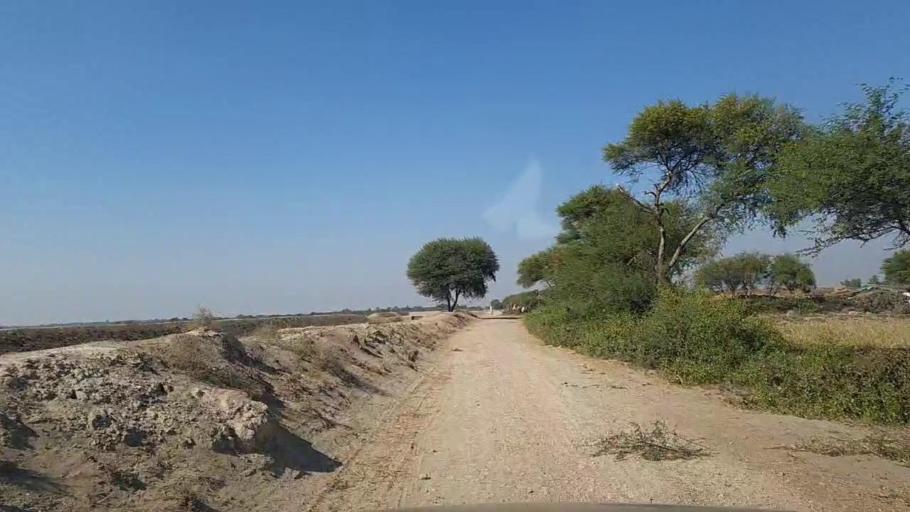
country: PK
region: Sindh
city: Mirpur Batoro
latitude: 24.7212
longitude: 68.2342
